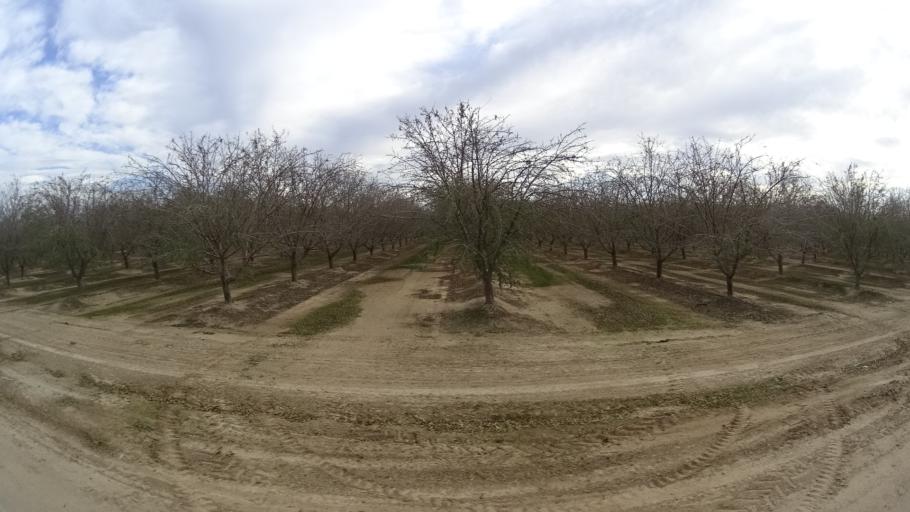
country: US
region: California
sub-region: Kern County
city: Rosedale
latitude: 35.4278
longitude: -119.1721
